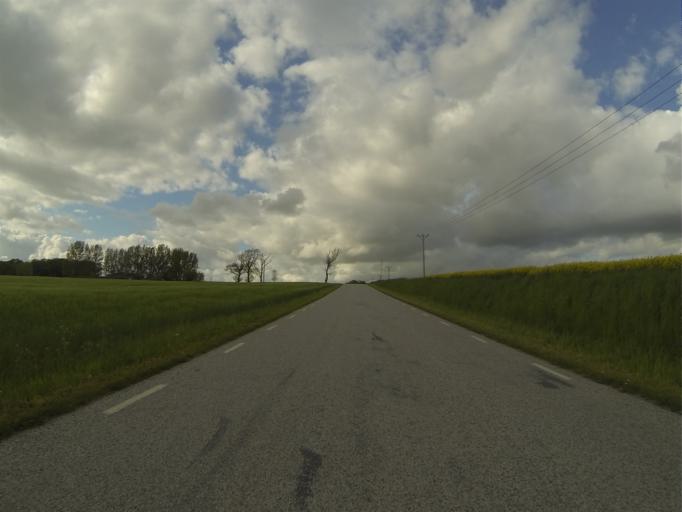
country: SE
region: Skane
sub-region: Staffanstorps Kommun
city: Staffanstorp
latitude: 55.6899
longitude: 13.2872
